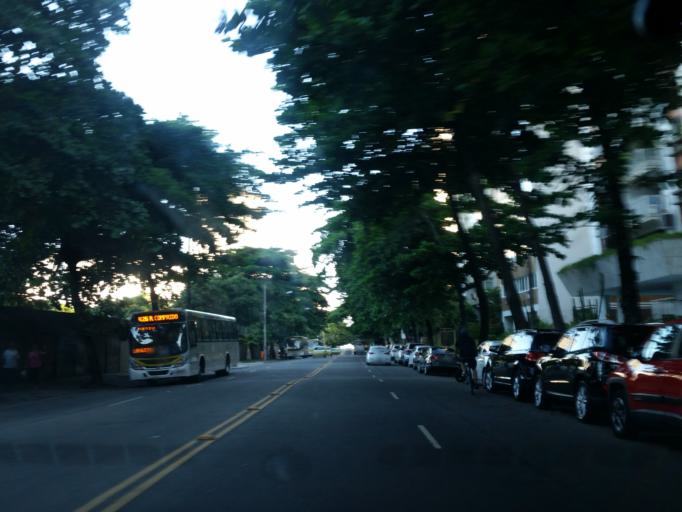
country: BR
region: Rio de Janeiro
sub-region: Rio De Janeiro
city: Rio de Janeiro
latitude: -22.9796
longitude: -43.2185
